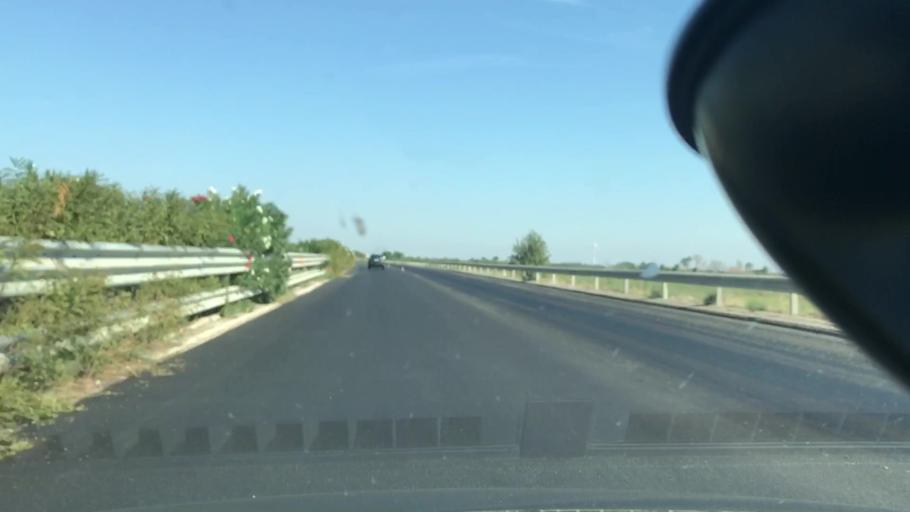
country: IT
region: Apulia
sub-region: Provincia di Foggia
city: Ascoli Satriano
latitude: 41.2768
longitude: 15.5537
